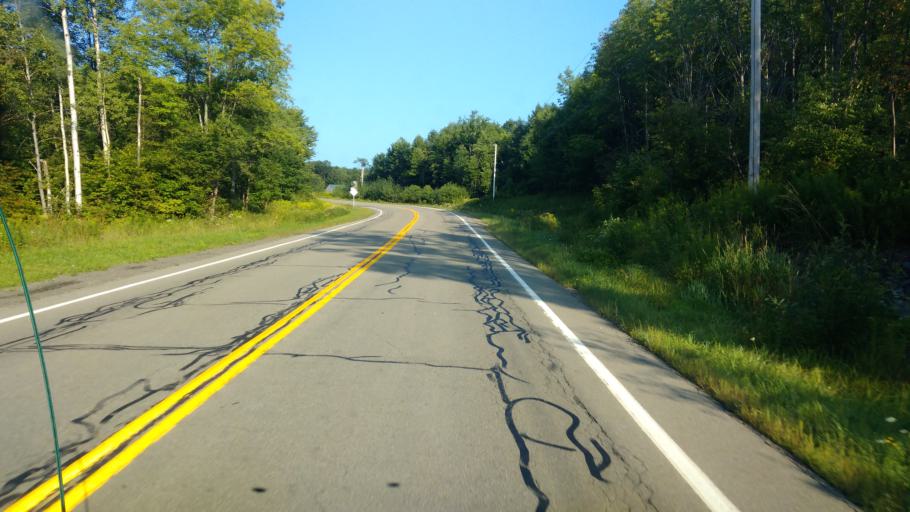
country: US
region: New York
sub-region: Allegany County
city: Andover
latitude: 42.1536
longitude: -77.6982
